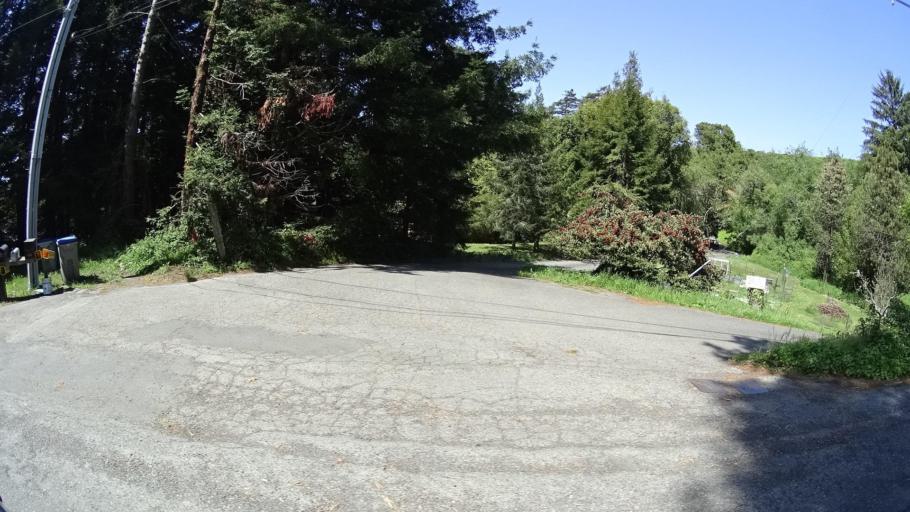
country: US
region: California
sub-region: Humboldt County
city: Fortuna
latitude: 40.5648
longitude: -124.1414
